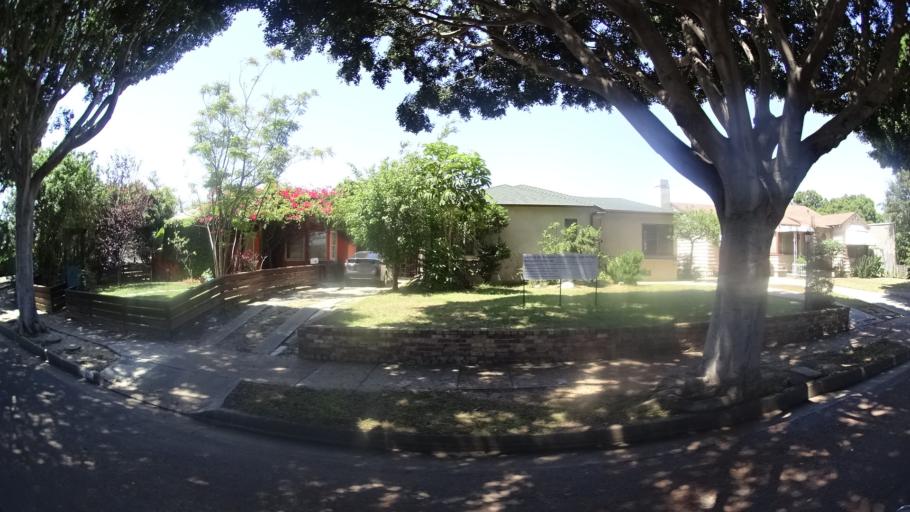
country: US
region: California
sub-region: Los Angeles County
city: Santa Monica
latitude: 34.0280
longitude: -118.4609
